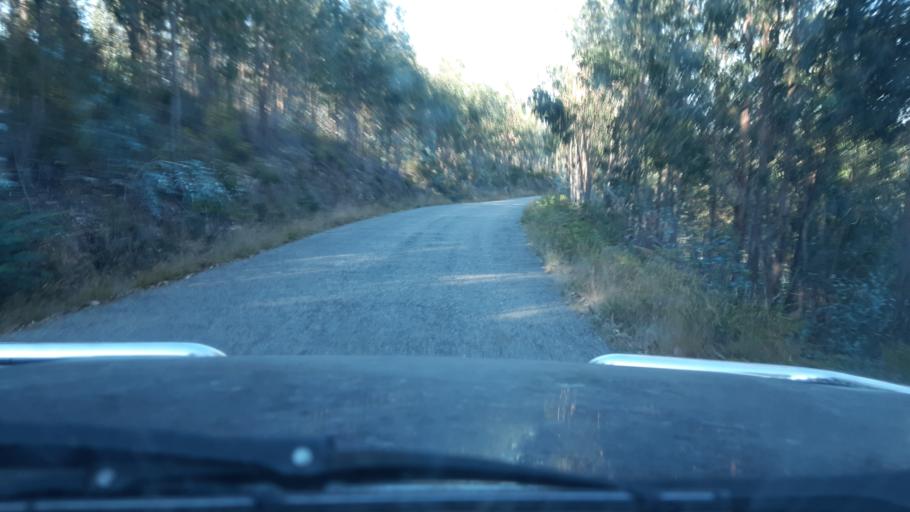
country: PT
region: Aveiro
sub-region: Agueda
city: Aguada de Cima
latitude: 40.5652
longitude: -8.3334
